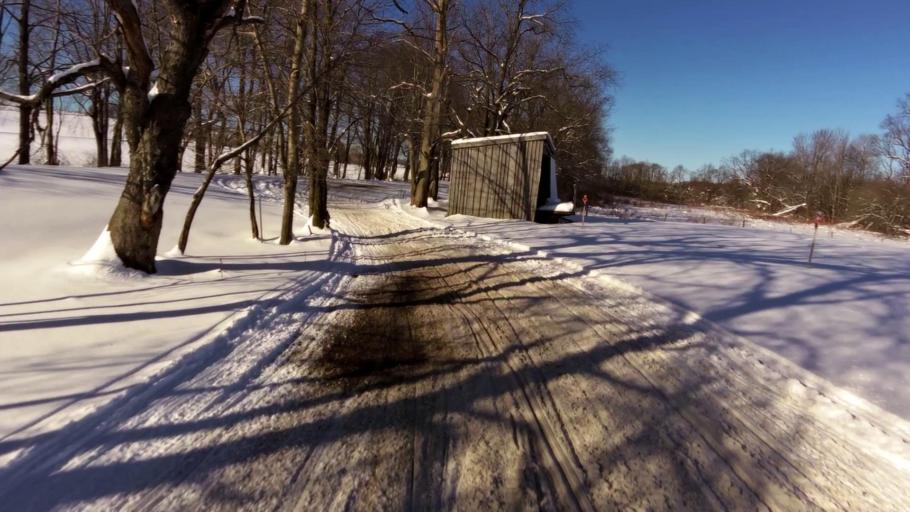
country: US
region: New York
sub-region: Chautauqua County
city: Mayville
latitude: 42.1700
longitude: -79.5831
